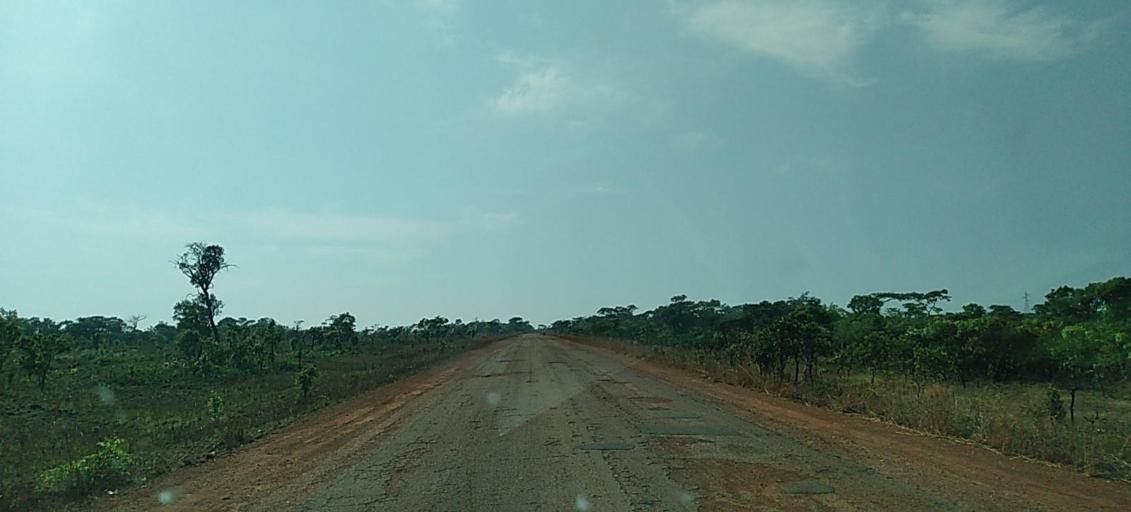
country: ZM
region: North-Western
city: Mwinilunga
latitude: -11.7746
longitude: 25.0164
